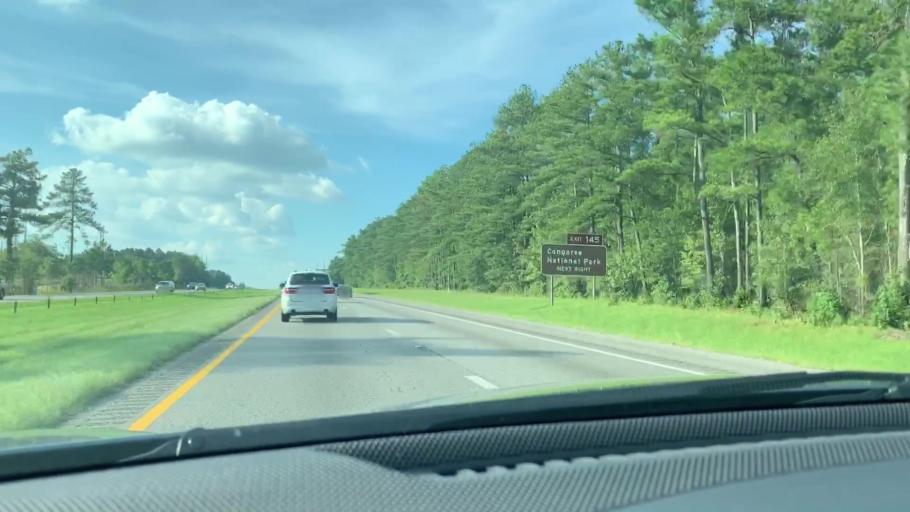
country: US
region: South Carolina
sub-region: Orangeburg County
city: Brookdale
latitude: 33.5537
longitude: -80.8194
